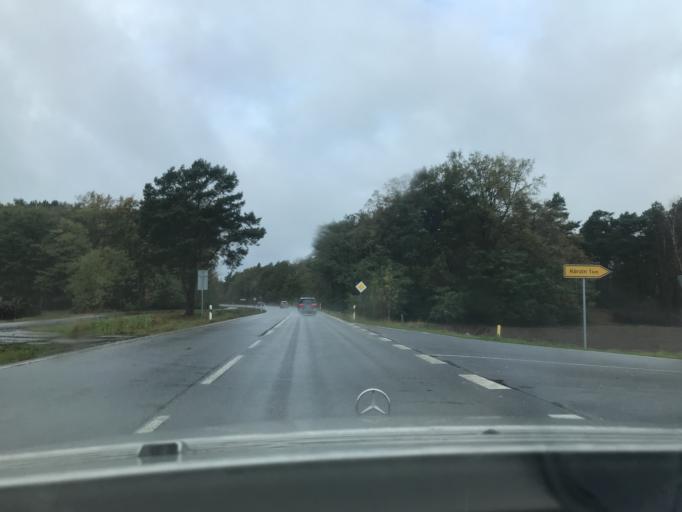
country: DE
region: Brandenburg
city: Michendorf
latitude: 52.2153
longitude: 13.0882
